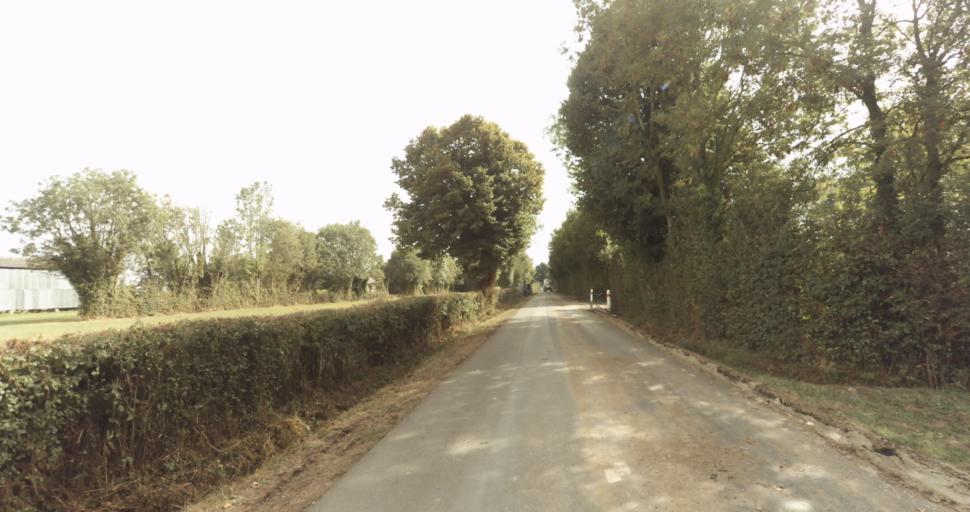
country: FR
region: Lower Normandy
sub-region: Departement de l'Orne
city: Gace
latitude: 48.8538
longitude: 0.2541
